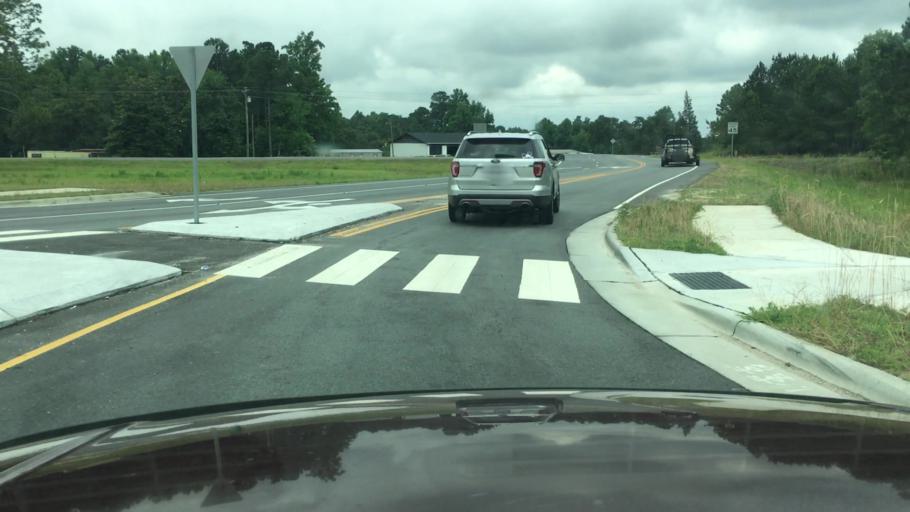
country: US
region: North Carolina
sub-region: Cumberland County
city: Spring Lake
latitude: 35.2587
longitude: -78.9706
